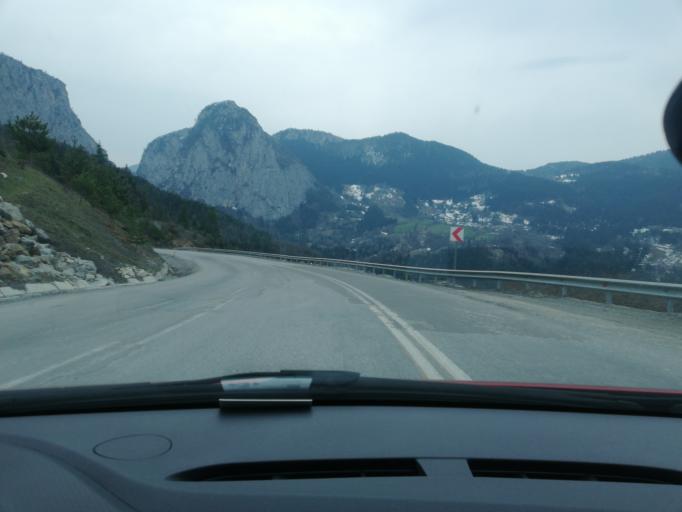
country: TR
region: Kastamonu
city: Kure
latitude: 41.8476
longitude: 33.7220
